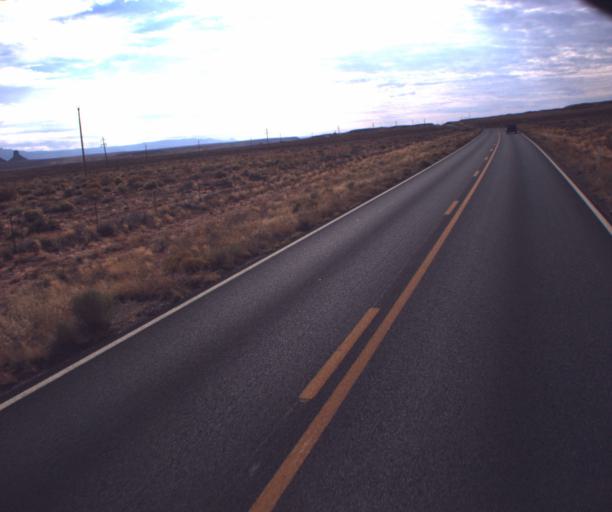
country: US
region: Arizona
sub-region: Apache County
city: Many Farms
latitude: 36.6144
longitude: -109.5791
